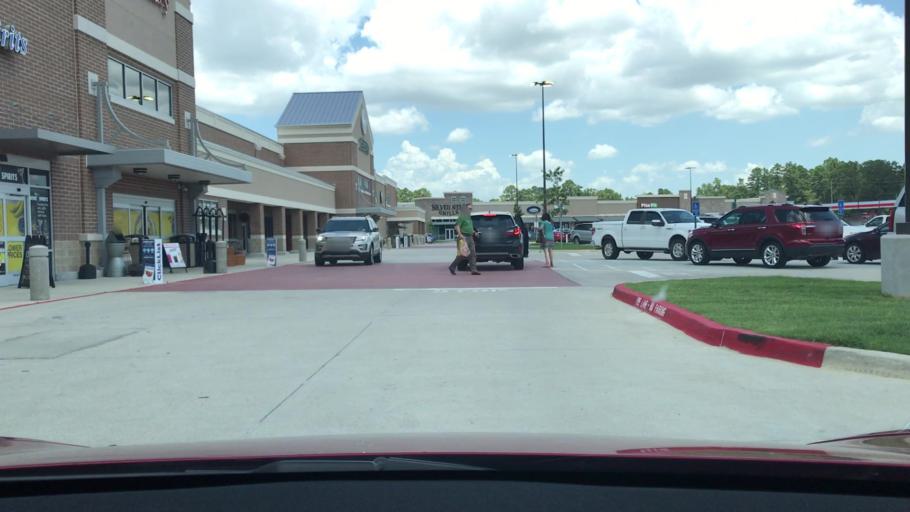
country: US
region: Louisiana
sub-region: Bossier Parish
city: Bossier City
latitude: 32.3935
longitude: -93.7283
